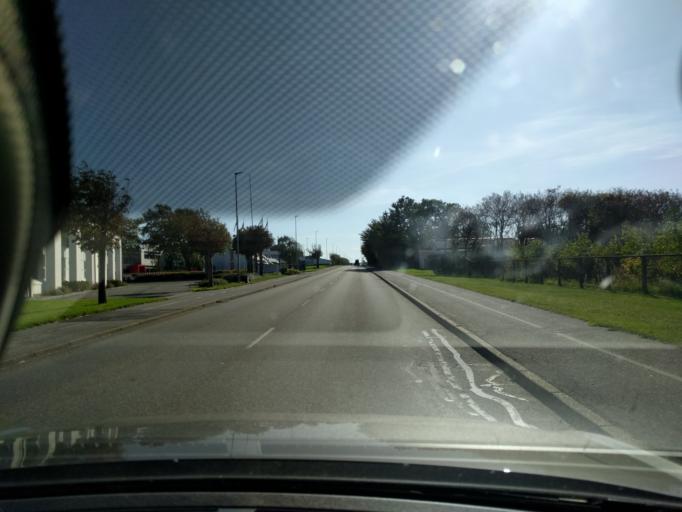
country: DK
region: North Denmark
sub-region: Vesthimmerland Kommune
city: Logstor
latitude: 56.9633
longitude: 9.2659
